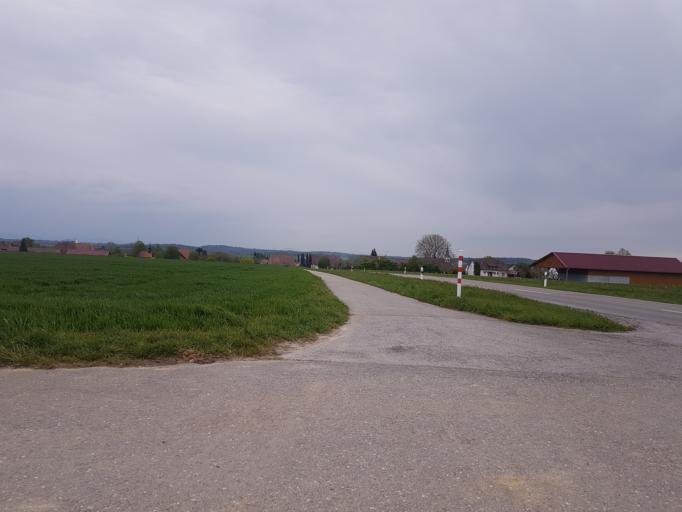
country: DE
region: Baden-Wuerttemberg
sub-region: Regierungsbezirk Stuttgart
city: Motzingen
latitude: 48.4729
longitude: 8.7796
